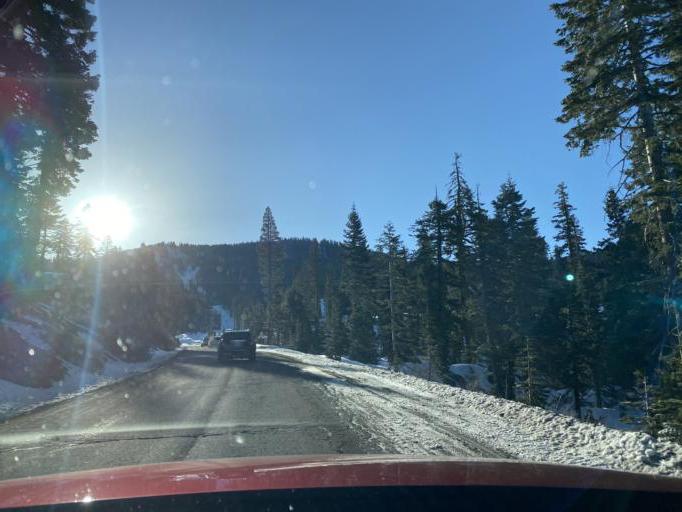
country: US
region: California
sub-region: El Dorado County
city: South Lake Tahoe
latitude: 38.8044
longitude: -120.0859
